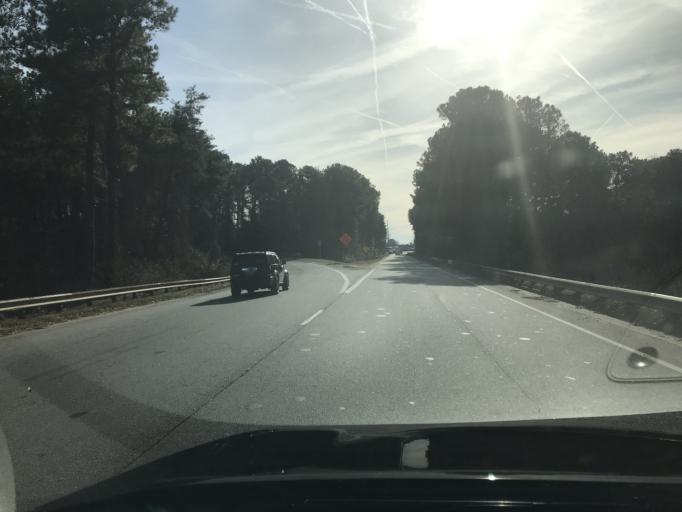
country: US
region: Georgia
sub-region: Clayton County
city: Forest Park
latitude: 33.6151
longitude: -84.3998
